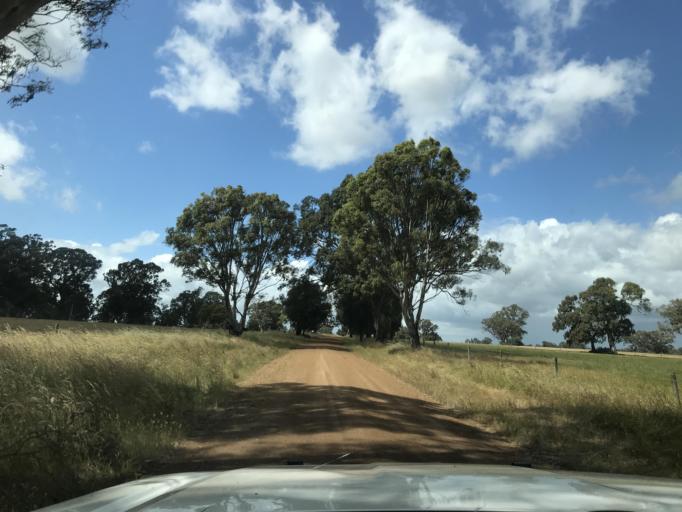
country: AU
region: South Australia
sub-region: Wattle Range
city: Penola
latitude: -37.1943
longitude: 141.4179
